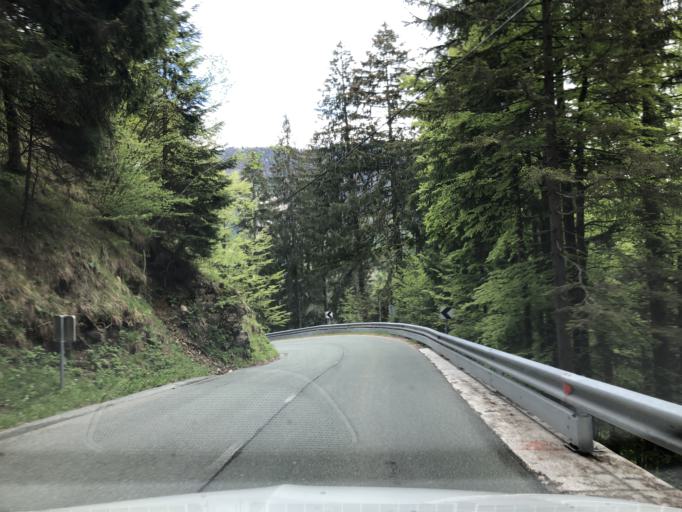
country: SI
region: Kranjska Gora
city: Kranjska Gora
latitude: 46.5003
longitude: 13.7560
